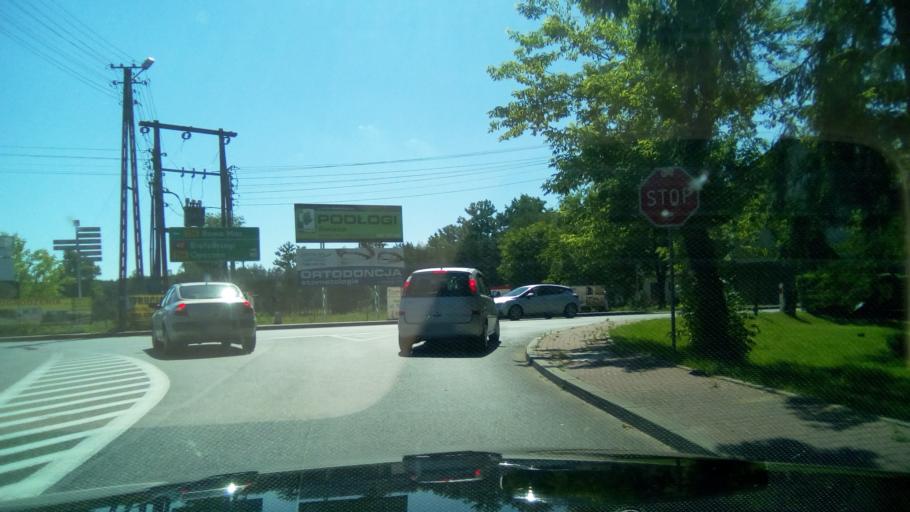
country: PL
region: Lodz Voivodeship
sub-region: Powiat tomaszowski
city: Inowlodz
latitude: 51.5258
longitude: 20.2229
